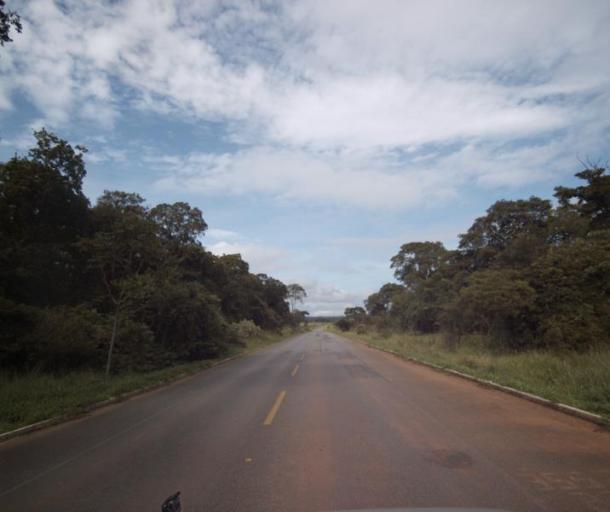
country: BR
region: Goias
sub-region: Pirenopolis
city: Pirenopolis
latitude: -15.6659
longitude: -48.6892
